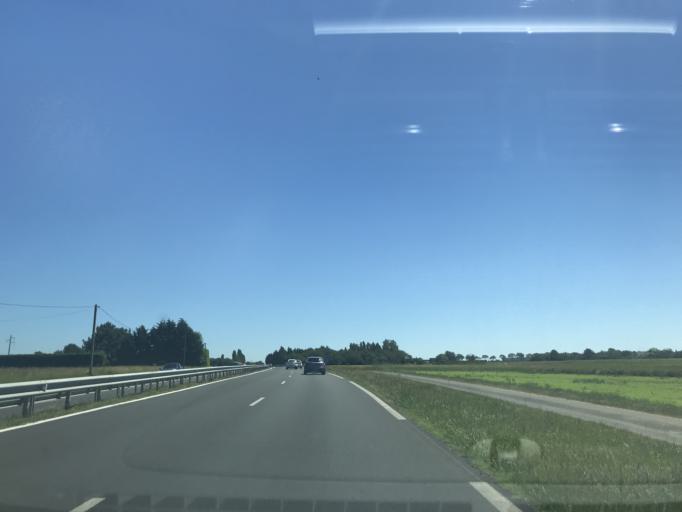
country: FR
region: Poitou-Charentes
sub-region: Departement de la Charente-Maritime
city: Vaux-sur-Mer
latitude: 45.6542
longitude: -1.0533
